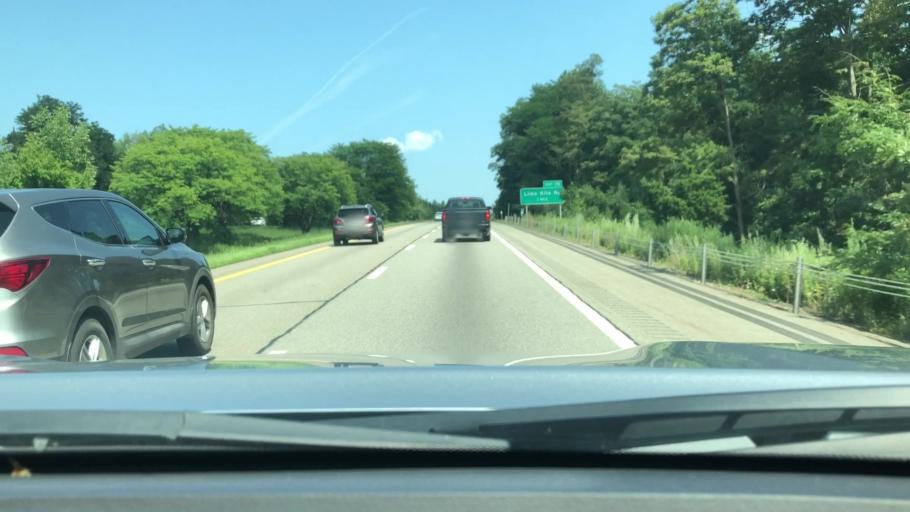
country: US
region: New York
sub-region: Dutchess County
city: Brinckerhoff
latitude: 41.5321
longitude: -73.8368
